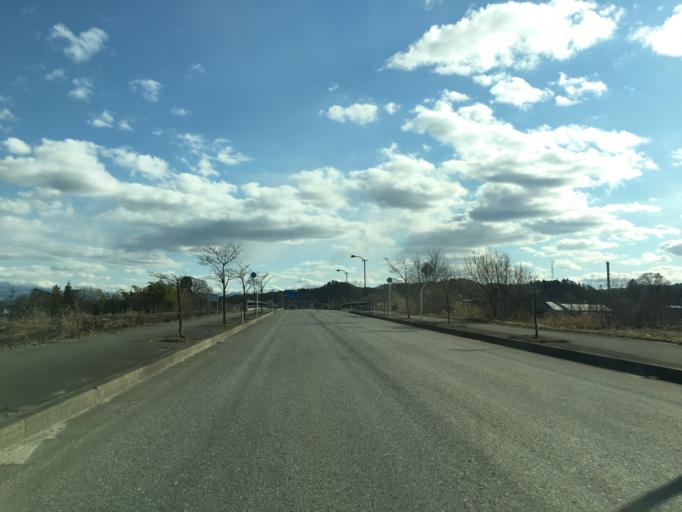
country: JP
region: Yamagata
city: Nagai
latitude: 38.0082
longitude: 140.0411
